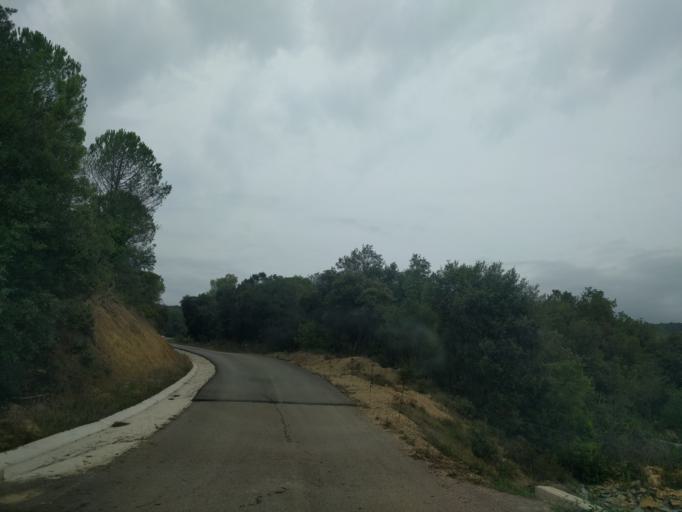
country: ES
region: Catalonia
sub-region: Provincia de Girona
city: la Cellera de Ter
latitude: 42.0178
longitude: 2.6343
